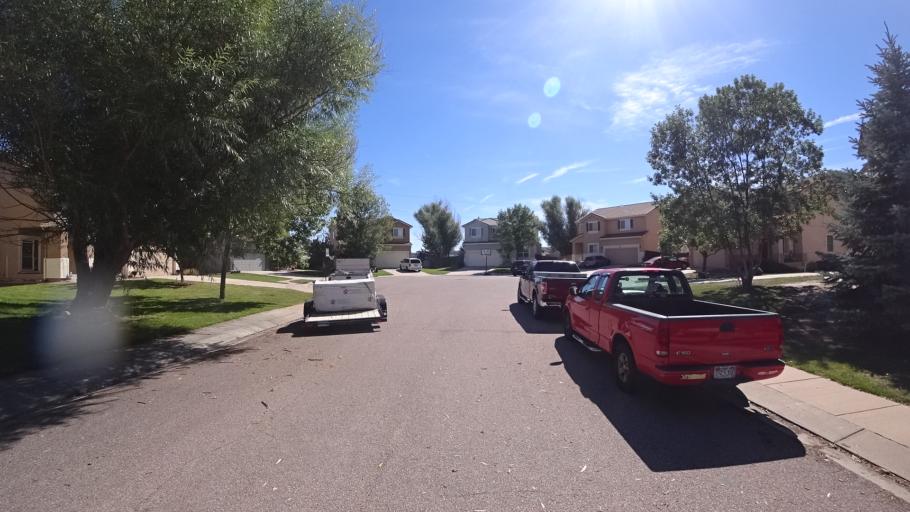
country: US
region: Colorado
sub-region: El Paso County
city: Black Forest
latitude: 38.9490
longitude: -104.7222
